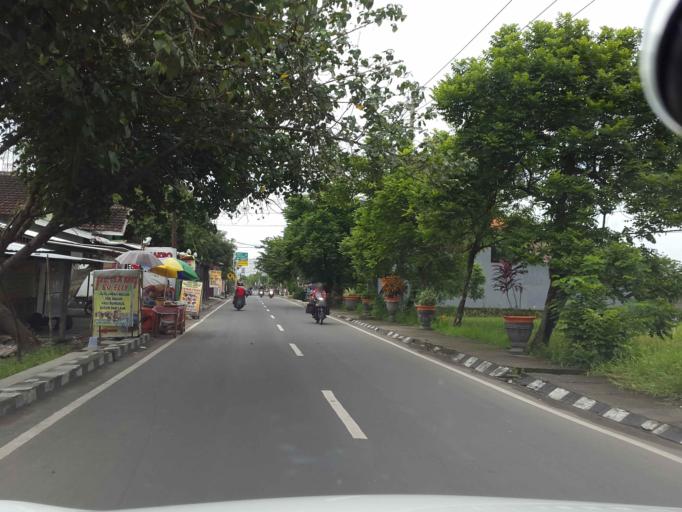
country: ID
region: East Java
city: Mojokerto
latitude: -7.4678
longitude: 112.4478
